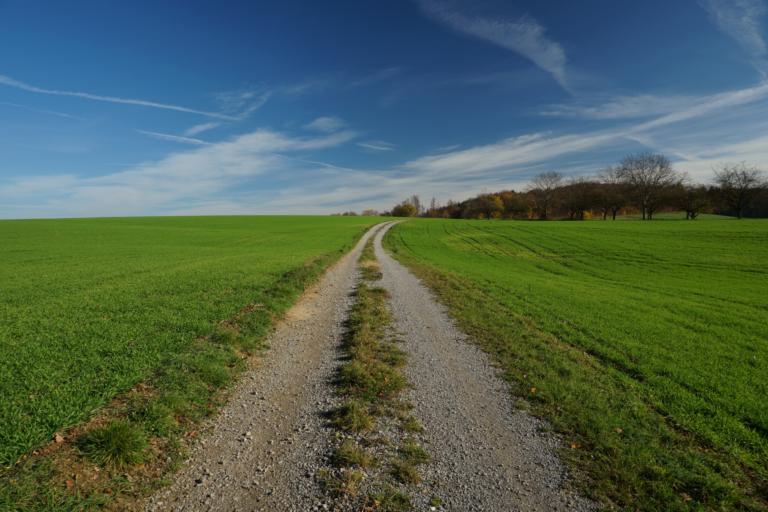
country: DE
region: Baden-Wuerttemberg
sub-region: Karlsruhe Region
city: Neunkirchen
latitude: 49.3603
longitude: 9.0169
